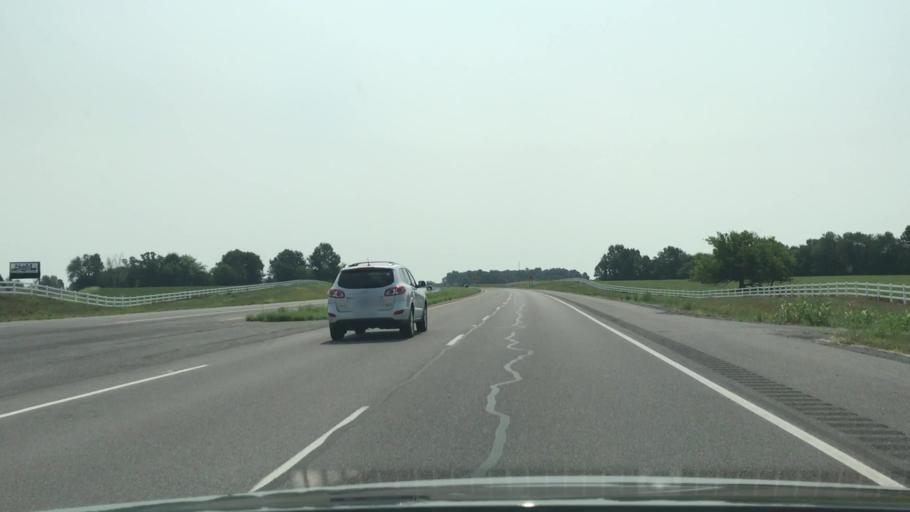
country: US
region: Kentucky
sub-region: Graves County
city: Mayfield
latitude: 36.6800
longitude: -88.5298
